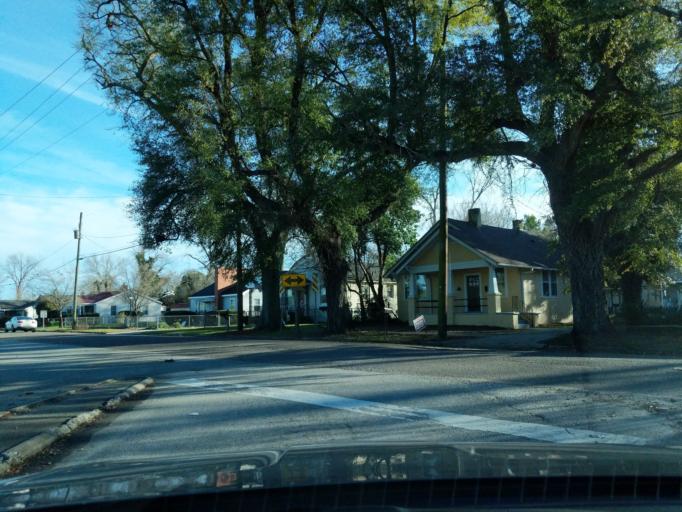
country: US
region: Georgia
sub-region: Richmond County
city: Augusta
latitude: 33.4723
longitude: -81.9529
